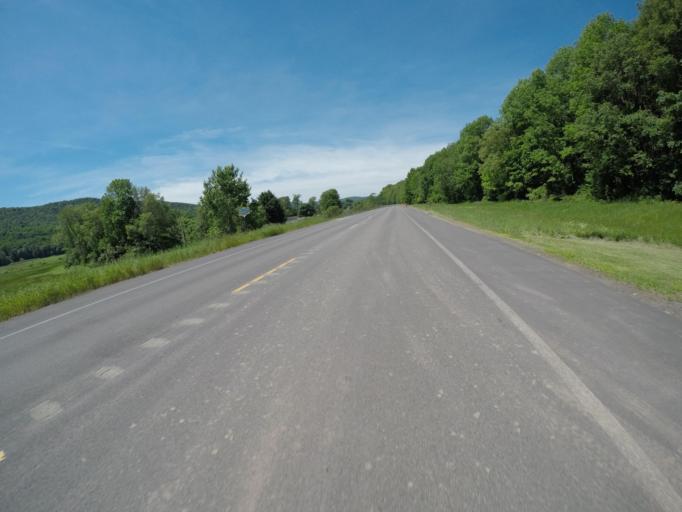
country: US
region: New York
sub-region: Delaware County
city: Walton
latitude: 42.1864
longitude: -75.0043
